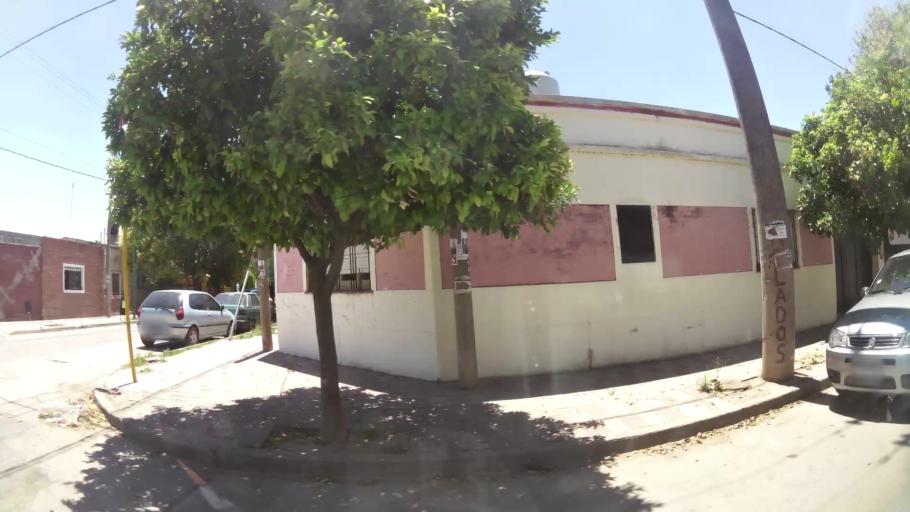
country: AR
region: Cordoba
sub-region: Departamento de Capital
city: Cordoba
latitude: -31.3794
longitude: -64.1348
